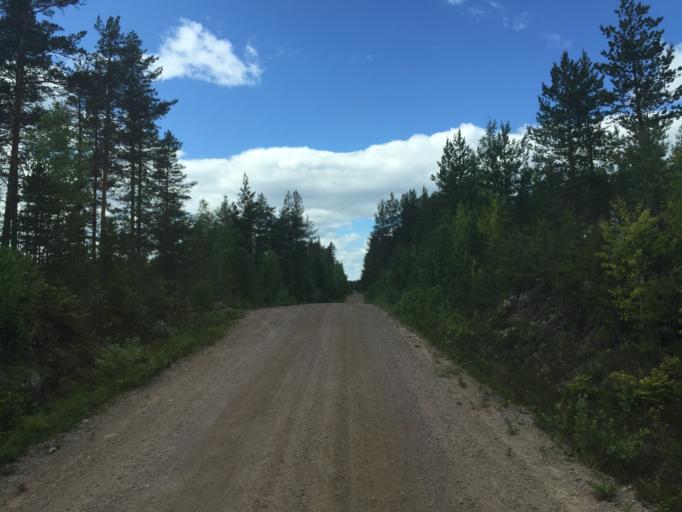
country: SE
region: Dalarna
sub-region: Vansbro Kommun
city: Vansbro
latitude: 60.4443
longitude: 14.1765
